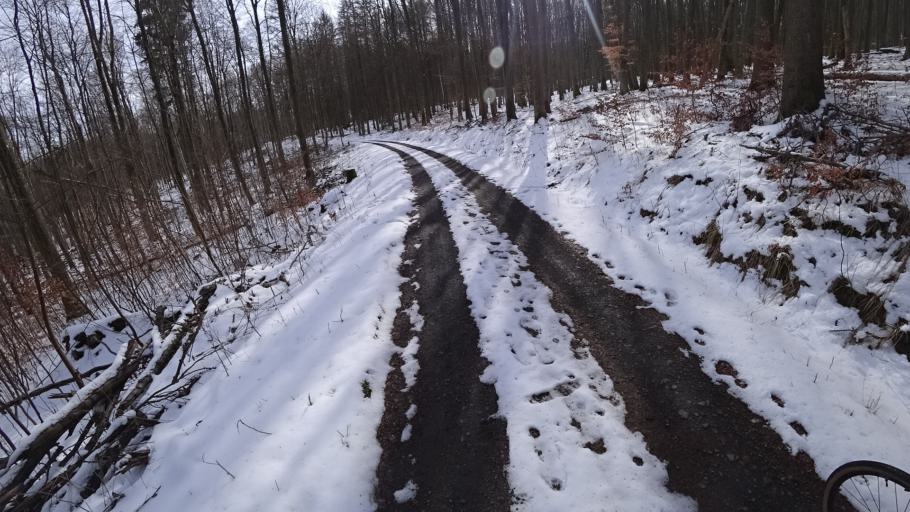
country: DE
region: Rheinland-Pfalz
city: Nauroth
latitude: 50.6841
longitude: 7.8677
